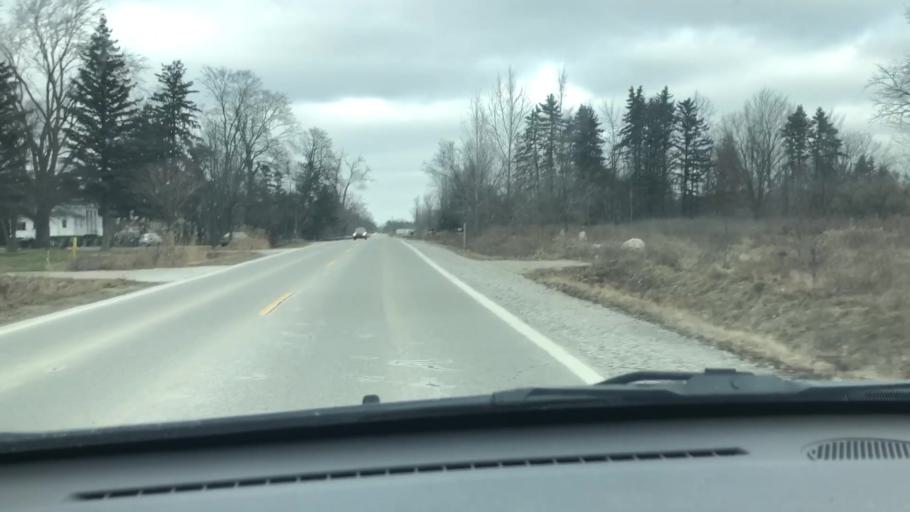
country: US
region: Michigan
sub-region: Macomb County
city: Romeo
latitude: 42.7374
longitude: -83.0172
